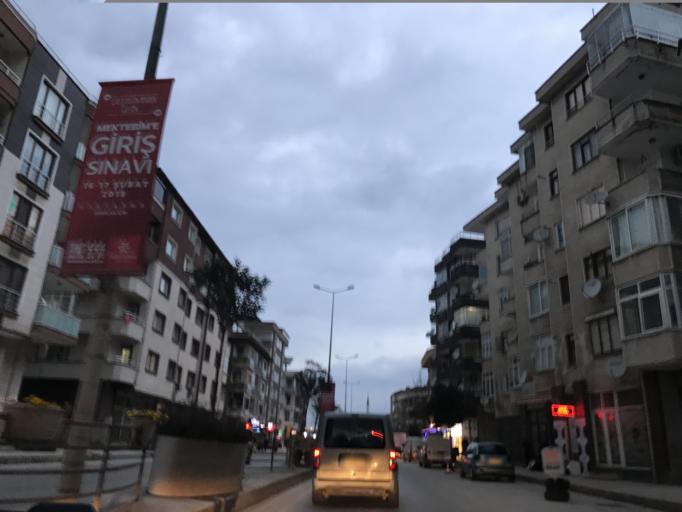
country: TR
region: Yalova
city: Yalova
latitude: 40.6522
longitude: 29.2579
